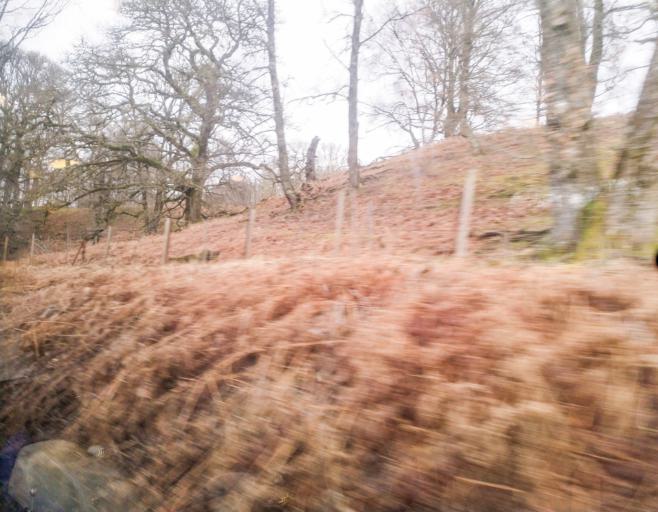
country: GB
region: Scotland
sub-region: Highland
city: Spean Bridge
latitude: 56.8931
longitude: -4.8893
